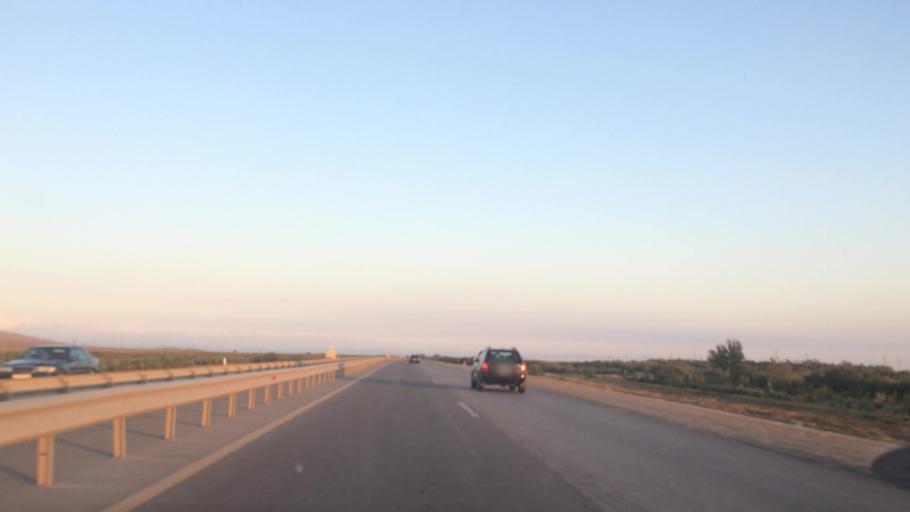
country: AZ
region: Baki
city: Qobustan
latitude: 39.9621
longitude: 49.2890
